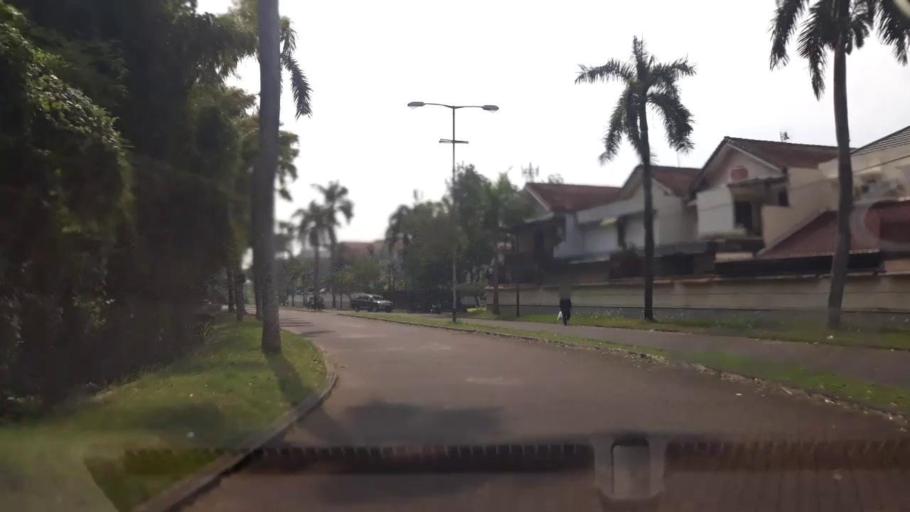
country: ID
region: Banten
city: Curug
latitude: -6.2242
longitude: 106.5867
